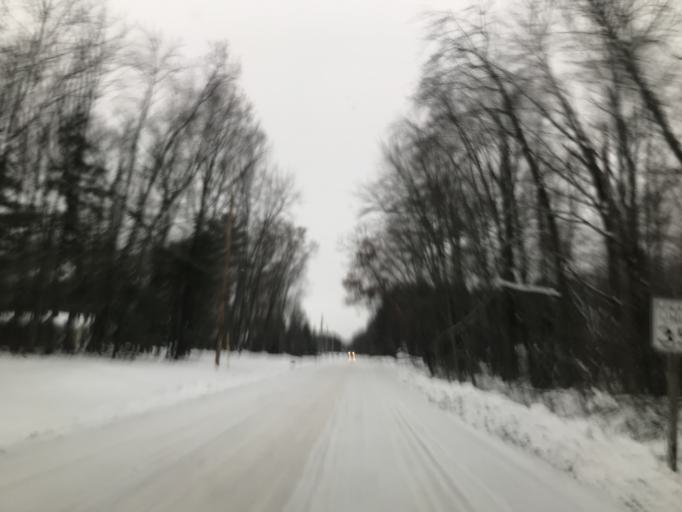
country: US
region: Wisconsin
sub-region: Marinette County
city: Peshtigo
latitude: 45.0398
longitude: -87.7192
